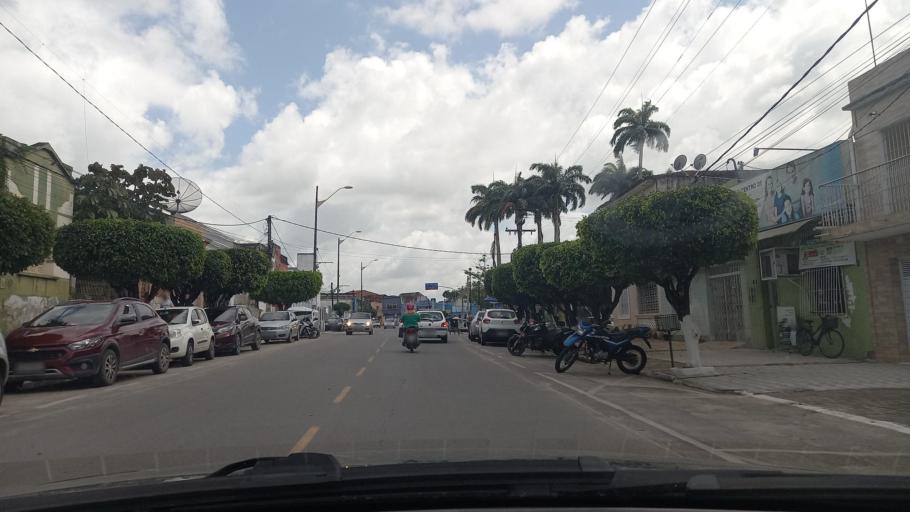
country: BR
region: Pernambuco
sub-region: Goiana
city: Goiana
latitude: -7.5578
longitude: -34.9995
